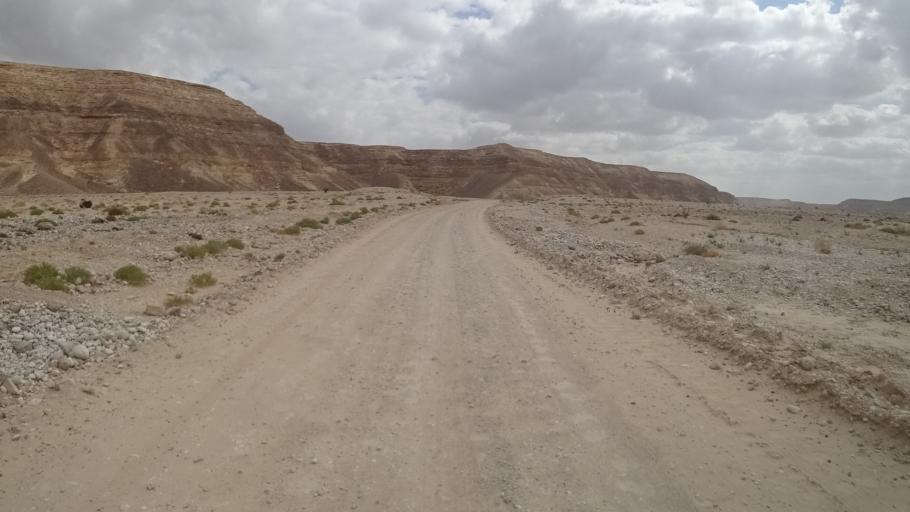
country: YE
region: Al Mahrah
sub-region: Shahan
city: Shihan as Sufla
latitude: 17.4625
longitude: 53.0075
